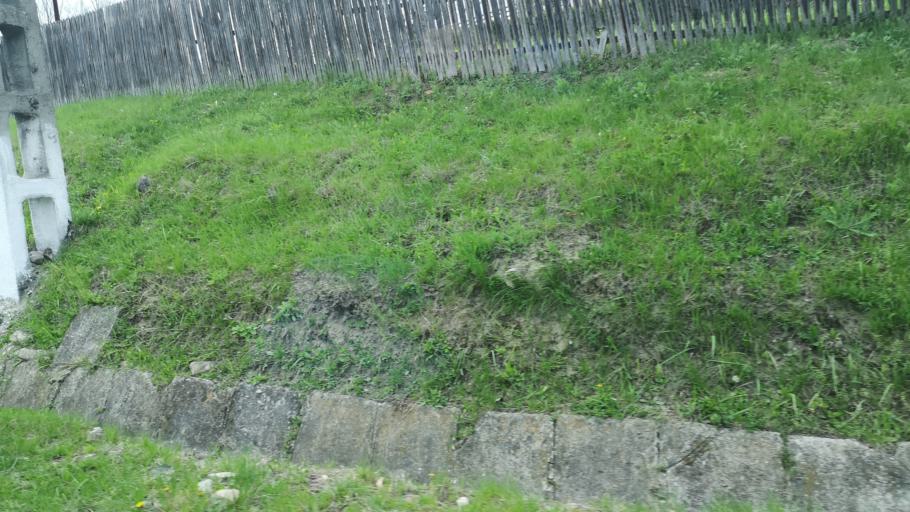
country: RO
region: Prahova
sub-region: Comuna Soimari
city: Soimari
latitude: 45.1562
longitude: 26.2038
